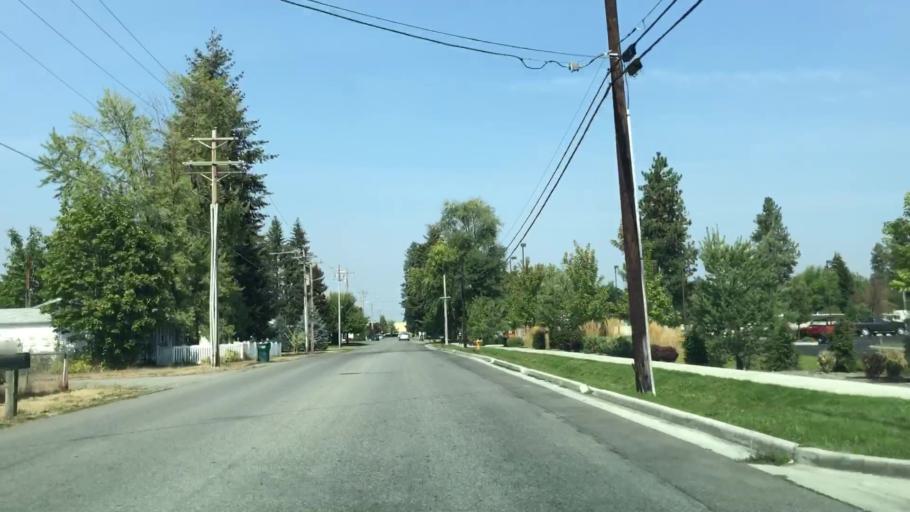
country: US
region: Idaho
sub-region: Kootenai County
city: Dalton Gardens
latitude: 47.7078
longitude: -116.7944
